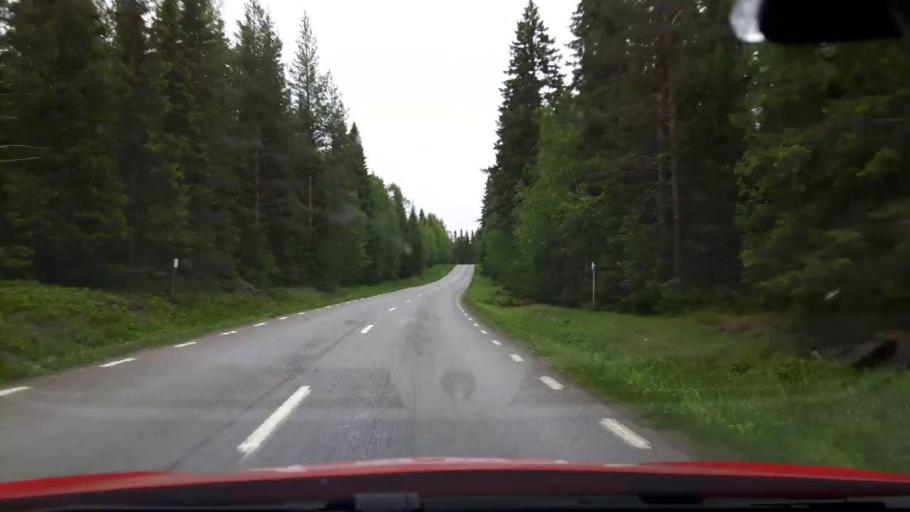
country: SE
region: Jaemtland
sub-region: Stroemsunds Kommun
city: Stroemsund
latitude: 63.4509
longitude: 15.4680
